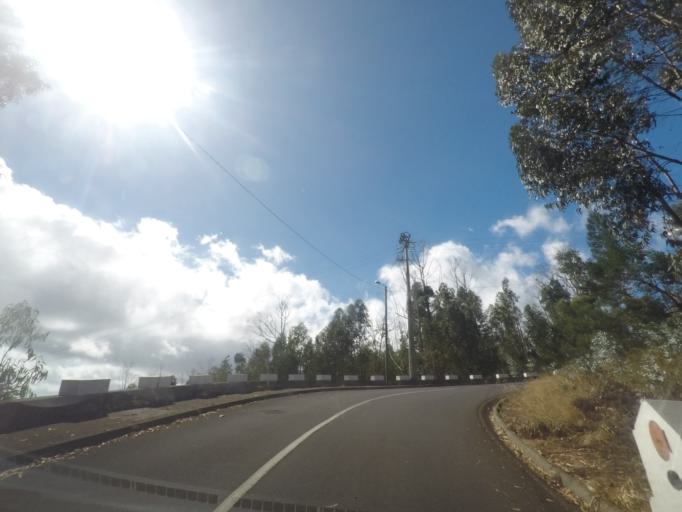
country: PT
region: Madeira
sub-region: Ribeira Brava
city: Campanario
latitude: 32.6871
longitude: -17.0397
